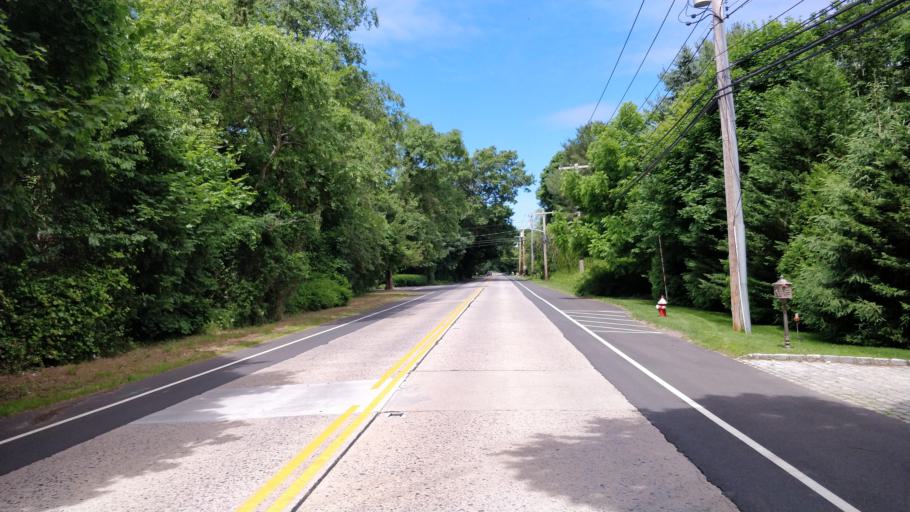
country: US
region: New York
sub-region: Nassau County
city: Laurel Hollow
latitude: 40.8418
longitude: -73.4794
